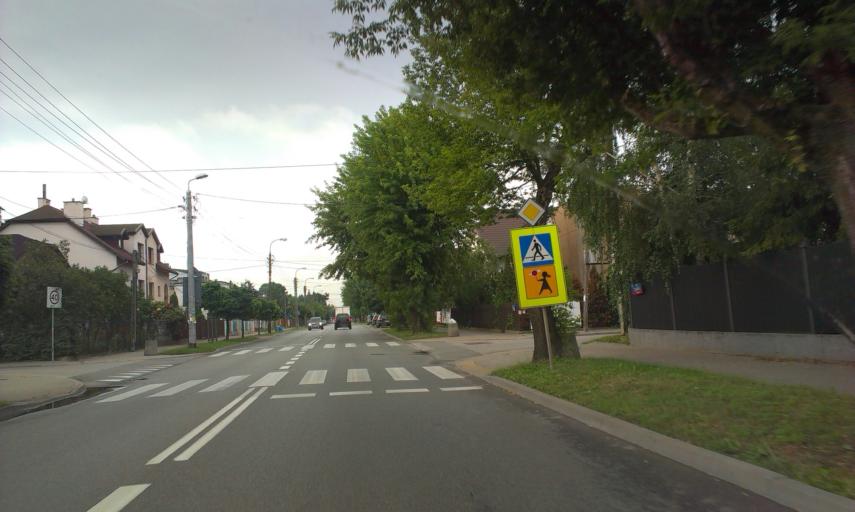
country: PL
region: Masovian Voivodeship
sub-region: Warszawa
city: Ursus
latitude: 52.1870
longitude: 20.8846
